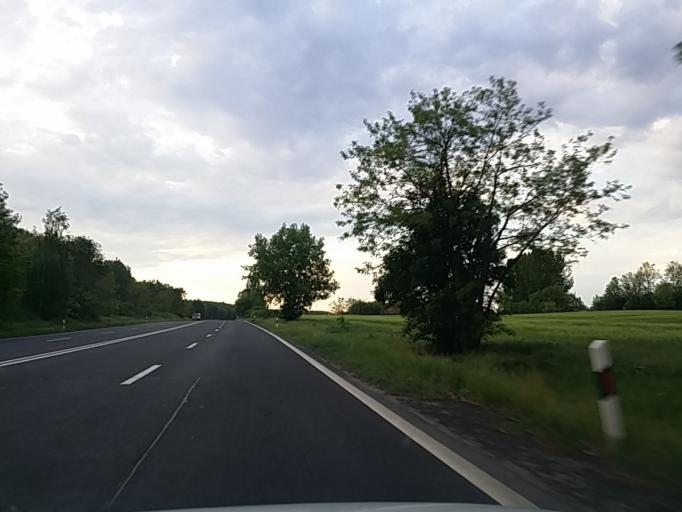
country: HU
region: Bacs-Kiskun
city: Lajosmizse
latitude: 46.9737
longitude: 19.6297
